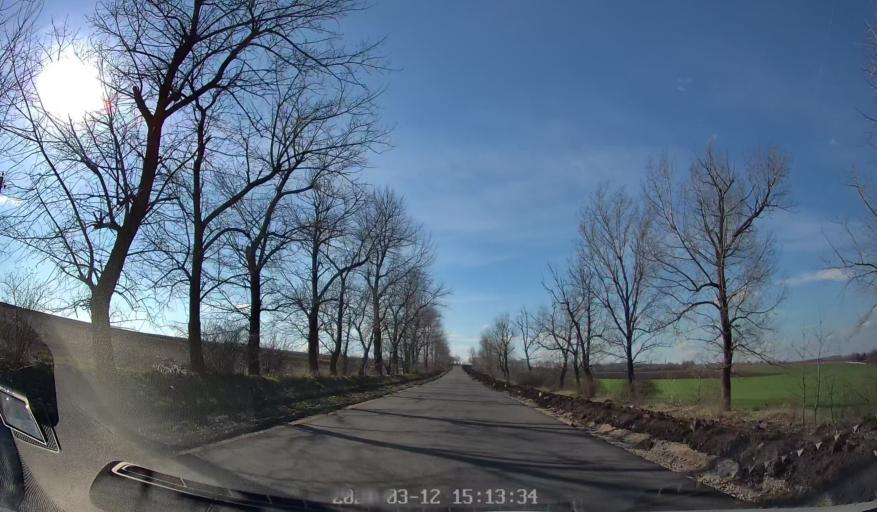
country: MD
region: Chisinau
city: Ciorescu
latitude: 47.2304
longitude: 28.9625
